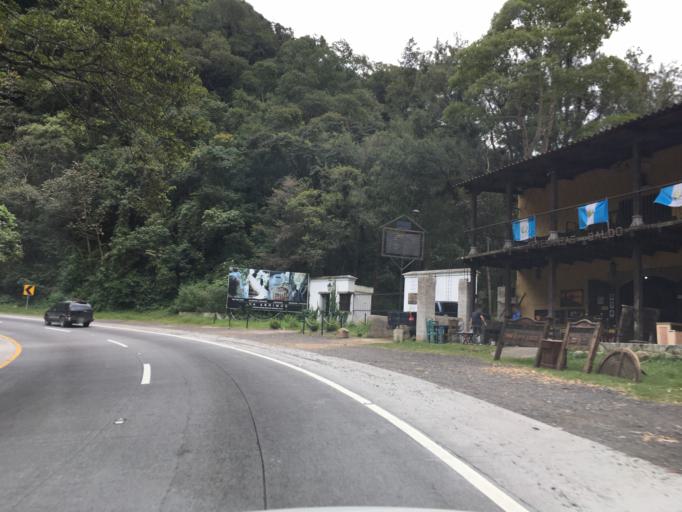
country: GT
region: Sacatepequez
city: Santa Lucia Milpas Altas
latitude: 14.5593
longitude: -90.6916
